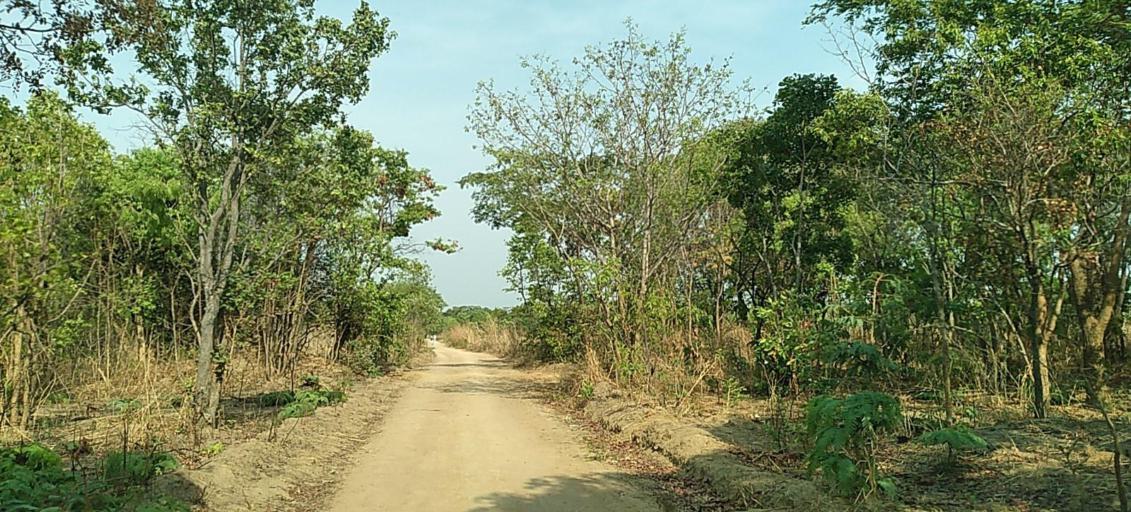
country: ZM
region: Copperbelt
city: Luanshya
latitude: -13.2195
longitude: 28.6602
